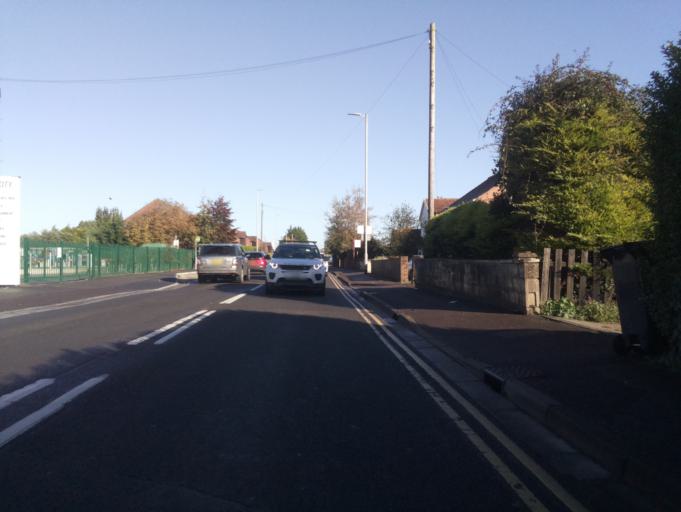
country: GB
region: England
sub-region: Somerset
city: Bridgwater
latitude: 51.1411
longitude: -2.9921
